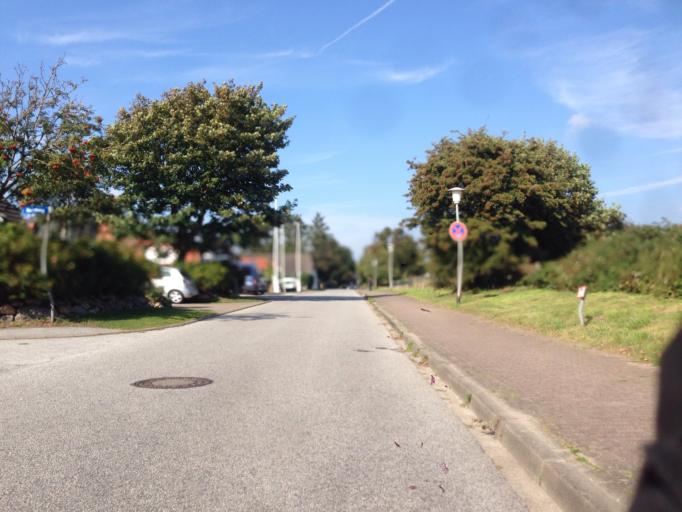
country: DE
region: Schleswig-Holstein
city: Westerland
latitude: 54.9067
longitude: 8.3187
